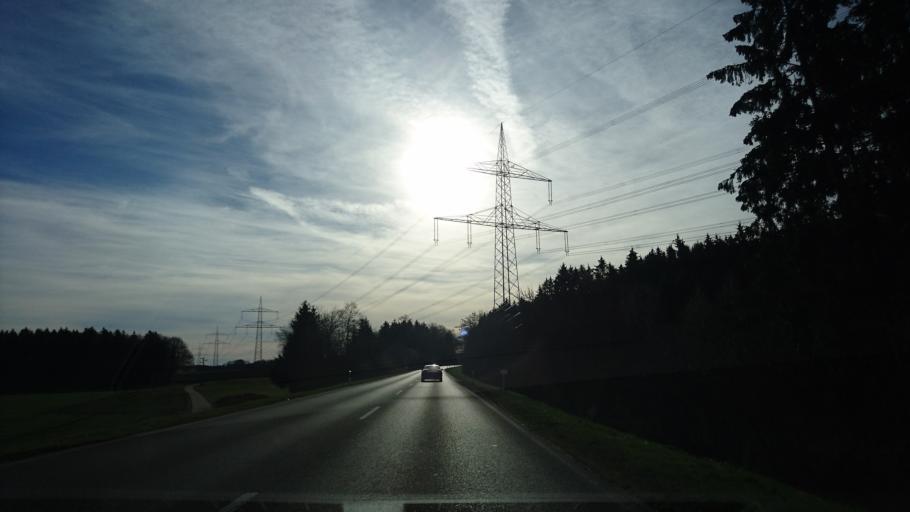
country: DE
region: Bavaria
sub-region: Swabia
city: Biberbach
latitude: 48.5284
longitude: 10.7737
